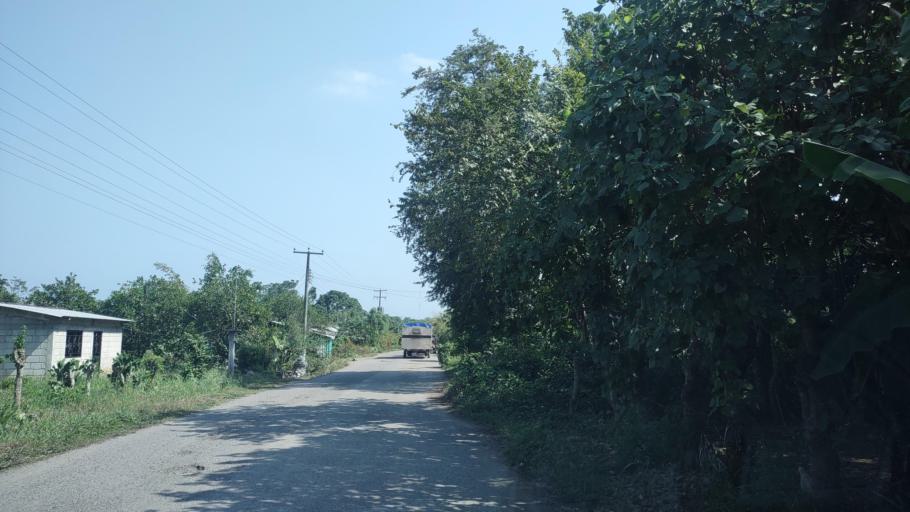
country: MX
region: Puebla
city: Espinal
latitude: 20.2542
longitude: -97.3324
